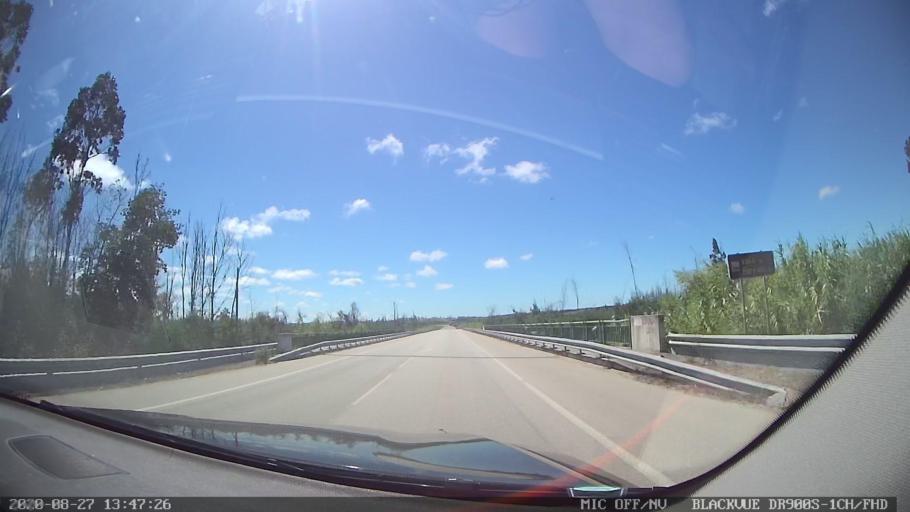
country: PT
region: Coimbra
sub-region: Mira
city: Mira
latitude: 40.3876
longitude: -8.7408
